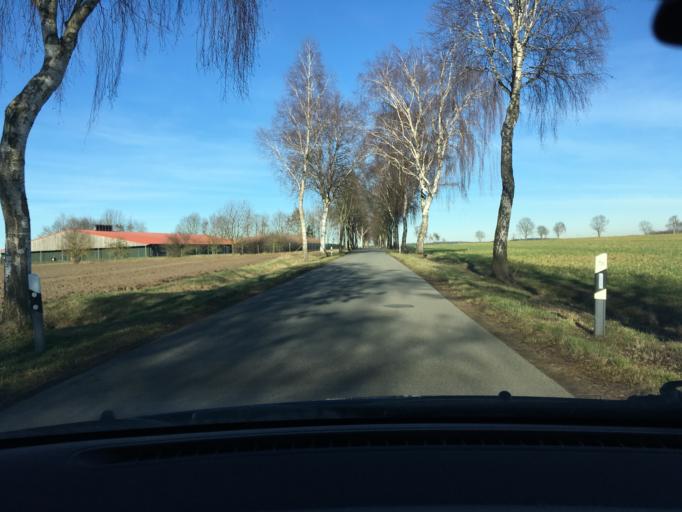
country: DE
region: Lower Saxony
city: Hanstedt Eins
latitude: 53.0354
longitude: 10.3697
